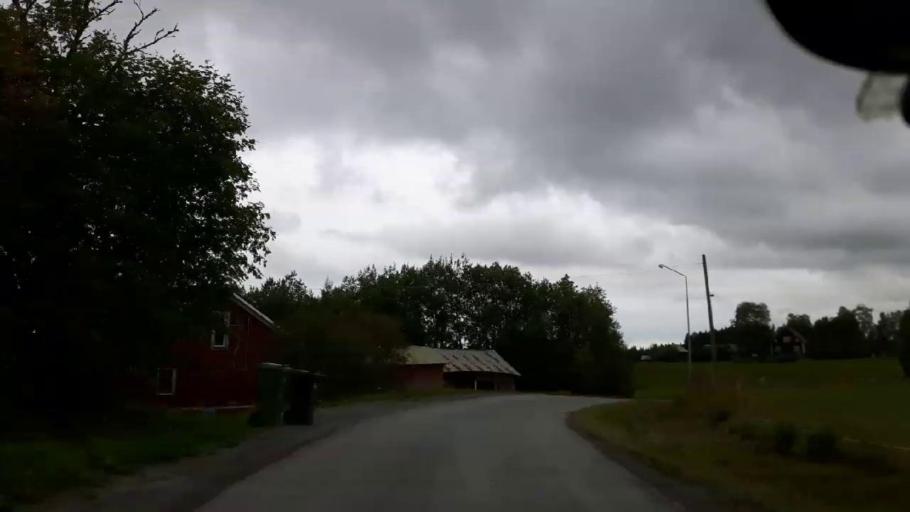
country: SE
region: Jaemtland
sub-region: OEstersunds Kommun
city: Ostersund
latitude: 63.0174
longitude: 14.5886
